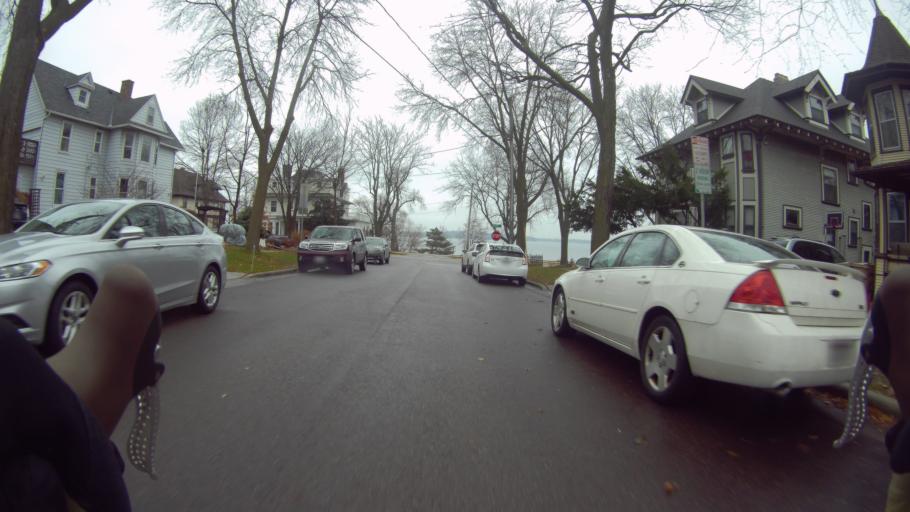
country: US
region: Wisconsin
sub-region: Dane County
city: Madison
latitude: 43.0786
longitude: -89.3684
